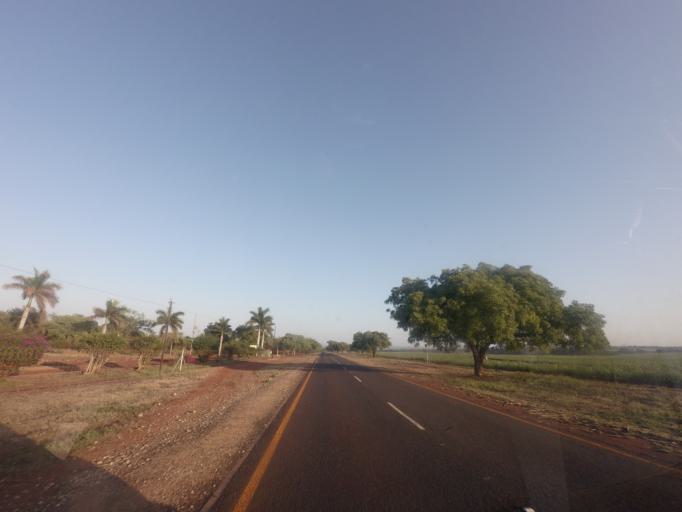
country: ZA
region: Mpumalanga
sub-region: Ehlanzeni District
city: Komatipoort
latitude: -25.3729
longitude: 31.9049
